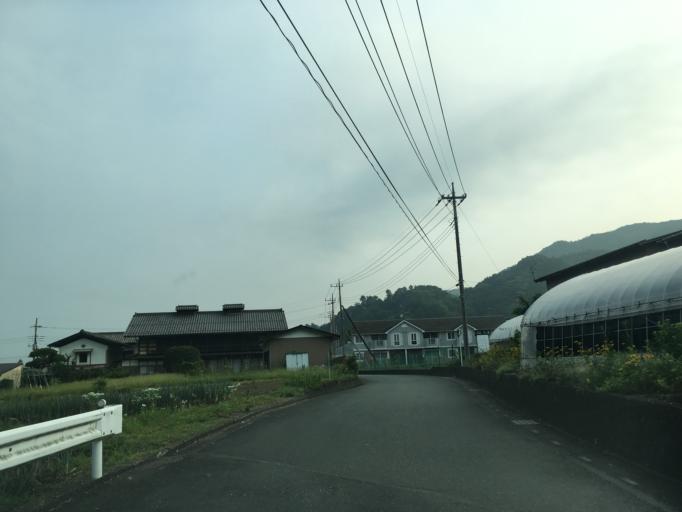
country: JP
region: Saitama
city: Chichibu
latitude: 35.9794
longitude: 139.1127
